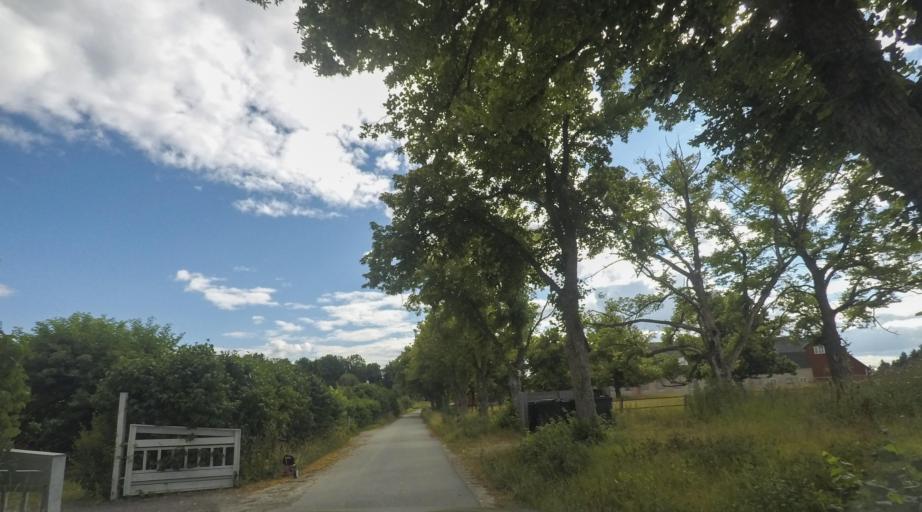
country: SE
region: Stockholm
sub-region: Sodertalje Kommun
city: Pershagen
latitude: 59.1142
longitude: 17.6594
